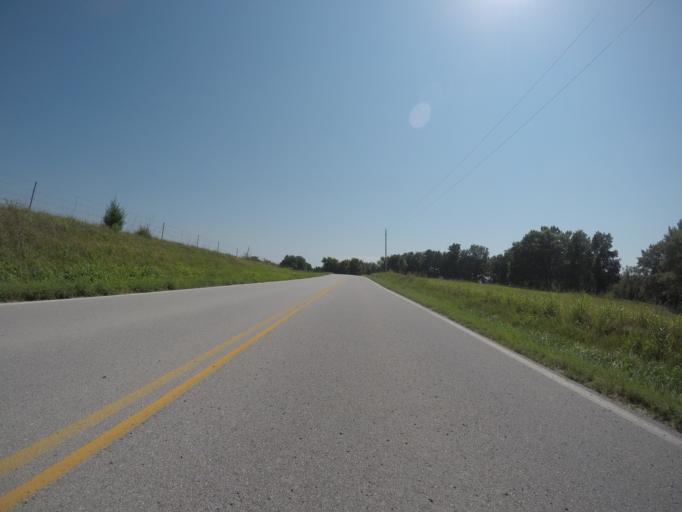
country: US
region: Kansas
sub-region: Leavenworth County
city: Lansing
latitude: 39.2503
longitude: -94.8762
